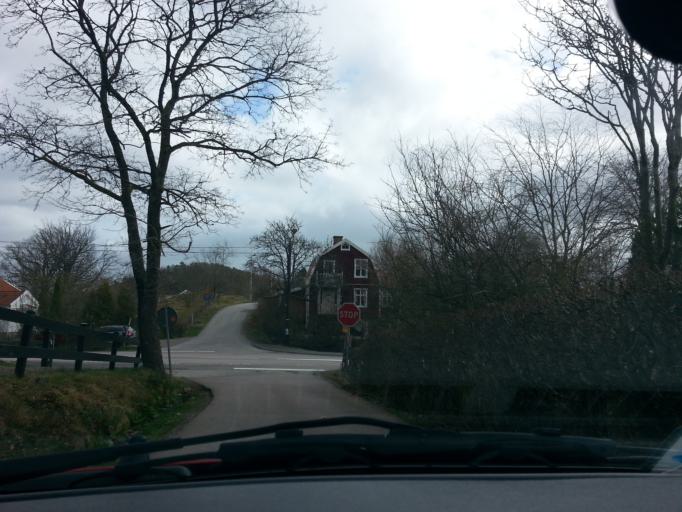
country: SE
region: Vaestra Goetaland
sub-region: Lerums Kommun
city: Grabo
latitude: 57.8747
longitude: 12.3268
